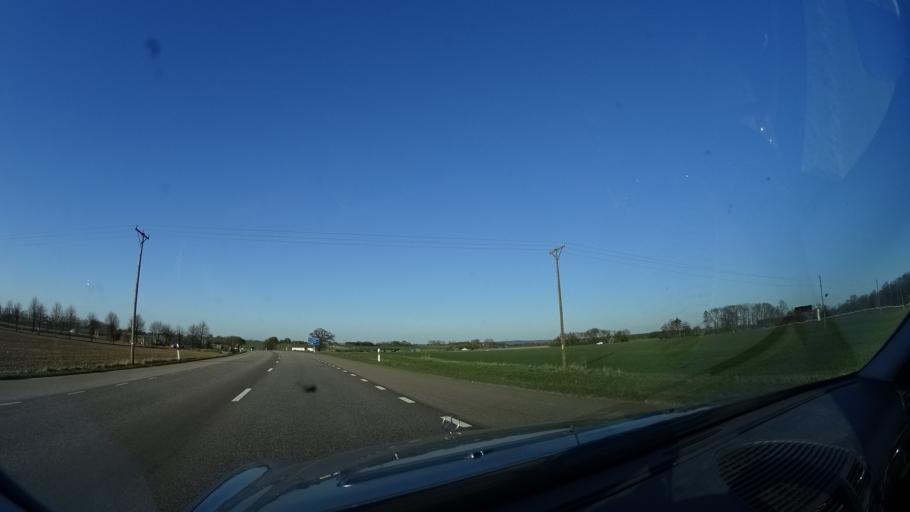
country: SE
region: Skane
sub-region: Helsingborg
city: Odakra
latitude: 56.0943
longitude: 12.7812
